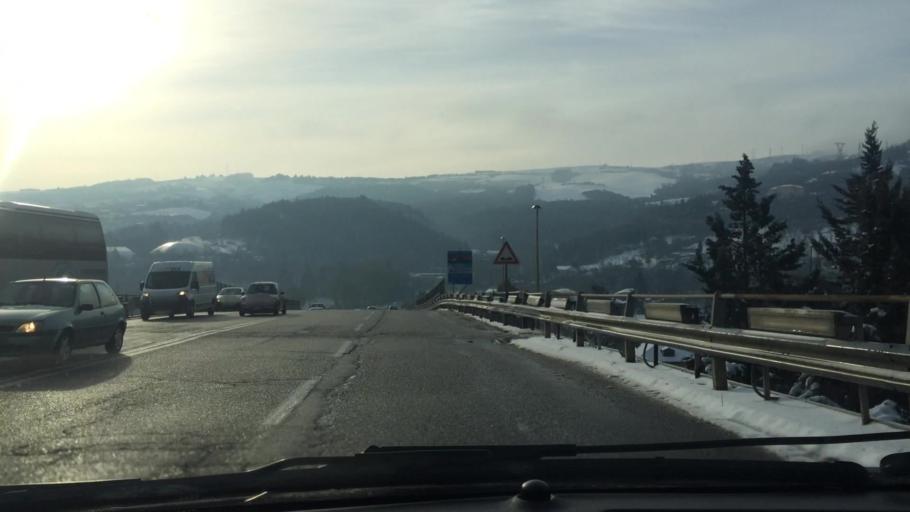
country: IT
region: Basilicate
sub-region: Provincia di Potenza
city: Potenza
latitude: 40.6288
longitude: 15.8044
